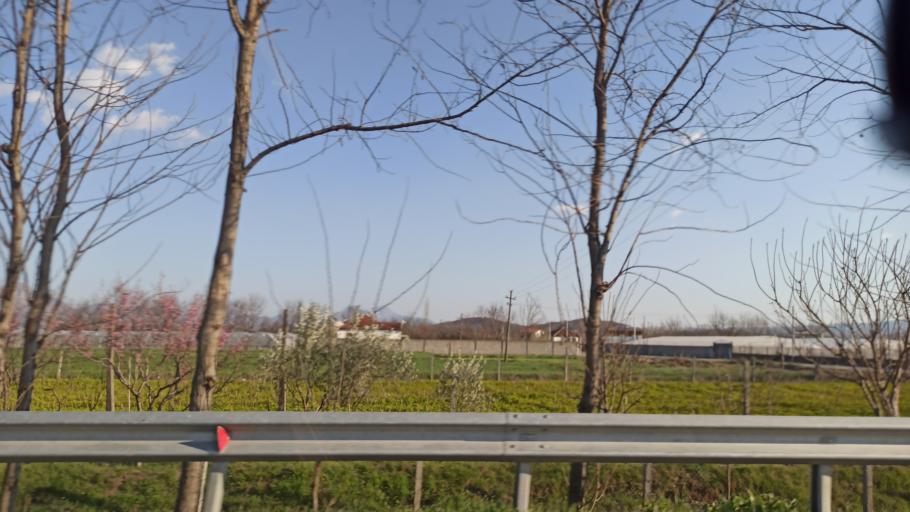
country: AL
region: Shkoder
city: Vukatane
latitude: 41.9913
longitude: 19.5559
